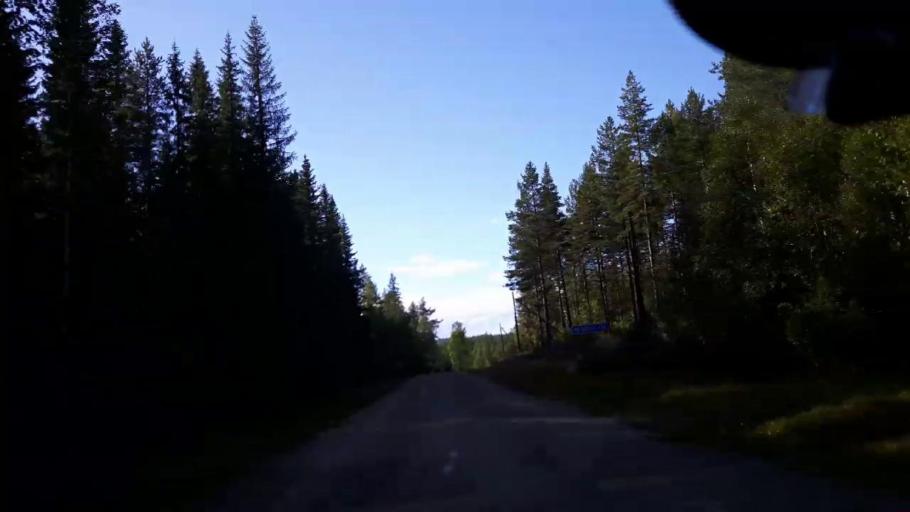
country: SE
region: Jaemtland
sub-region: Ragunda Kommun
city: Hammarstrand
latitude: 63.4821
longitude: 16.1176
